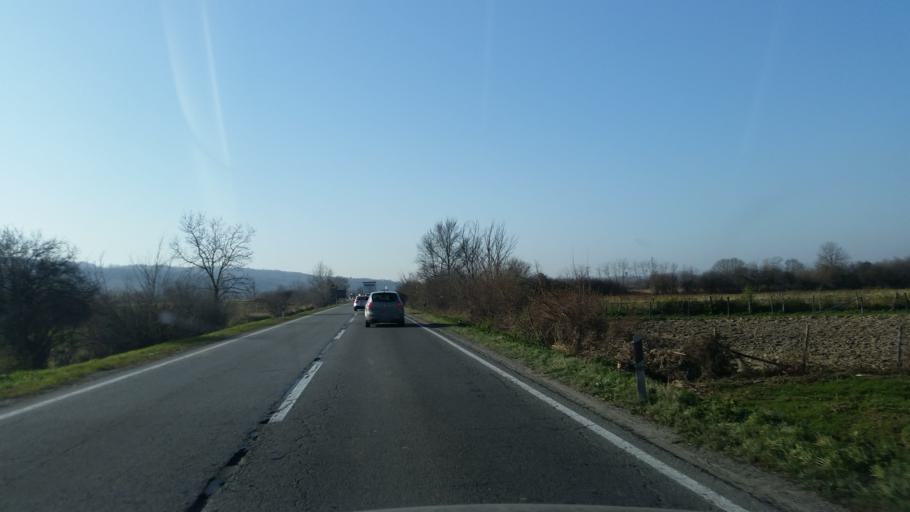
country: RS
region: Central Serbia
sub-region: Belgrade
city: Lazarevac
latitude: 44.3790
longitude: 20.2265
